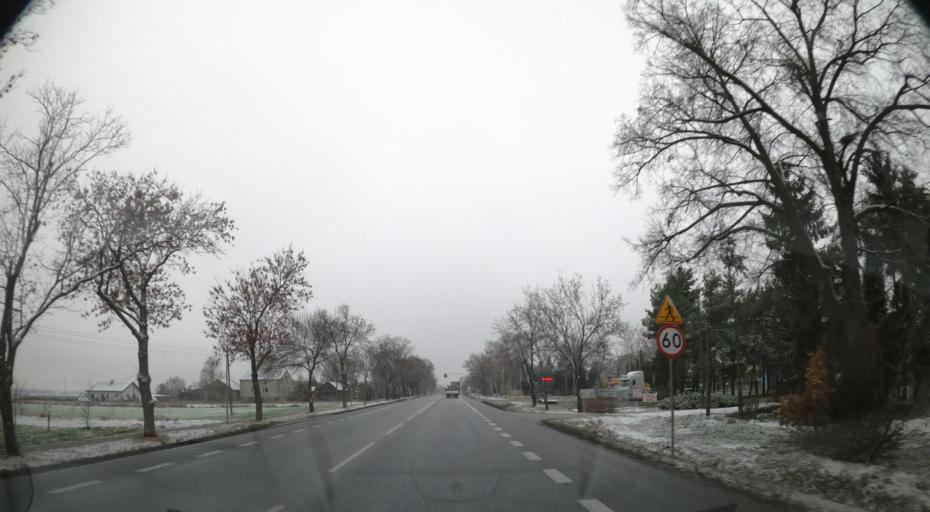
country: PL
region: Masovian Voivodeship
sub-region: Powiat warszawski zachodni
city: Blonie
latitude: 52.1997
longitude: 20.5910
